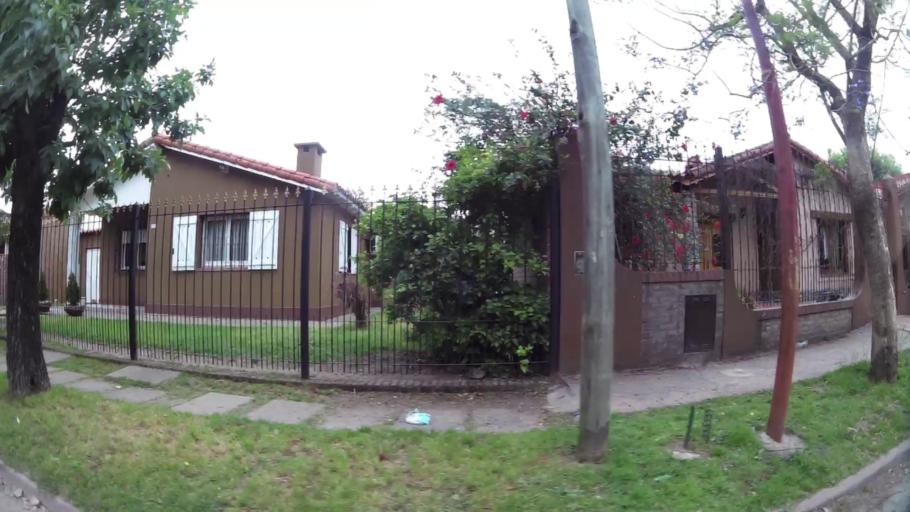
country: AR
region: Buenos Aires
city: San Justo
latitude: -34.7140
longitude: -58.5354
